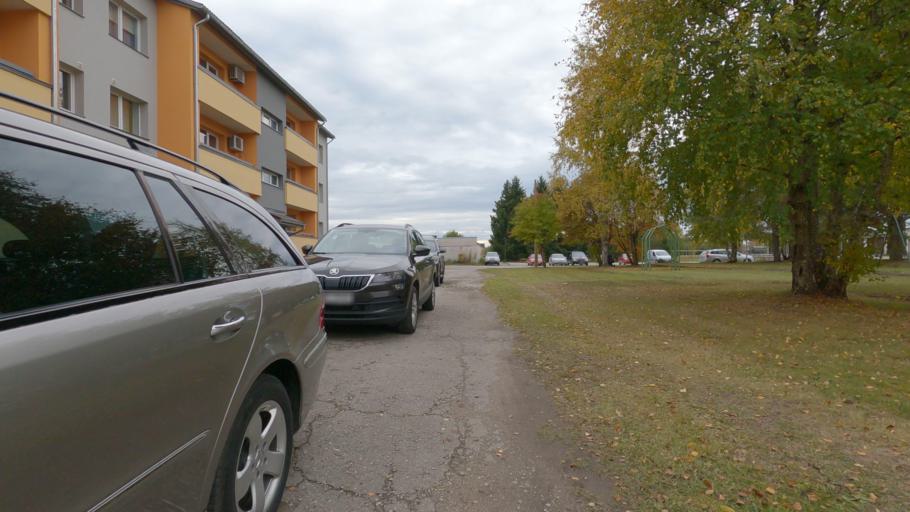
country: EE
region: Raplamaa
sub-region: Rapla vald
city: Rapla
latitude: 58.9961
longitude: 24.7928
